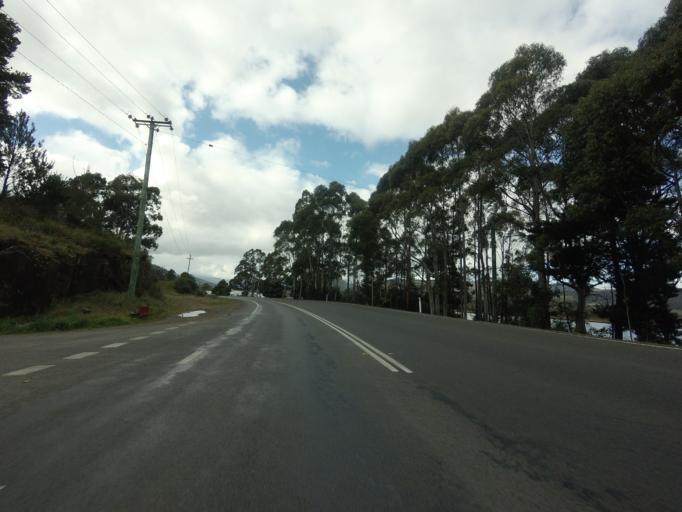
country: AU
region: Tasmania
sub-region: Huon Valley
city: Franklin
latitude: -43.1097
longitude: 147.0001
